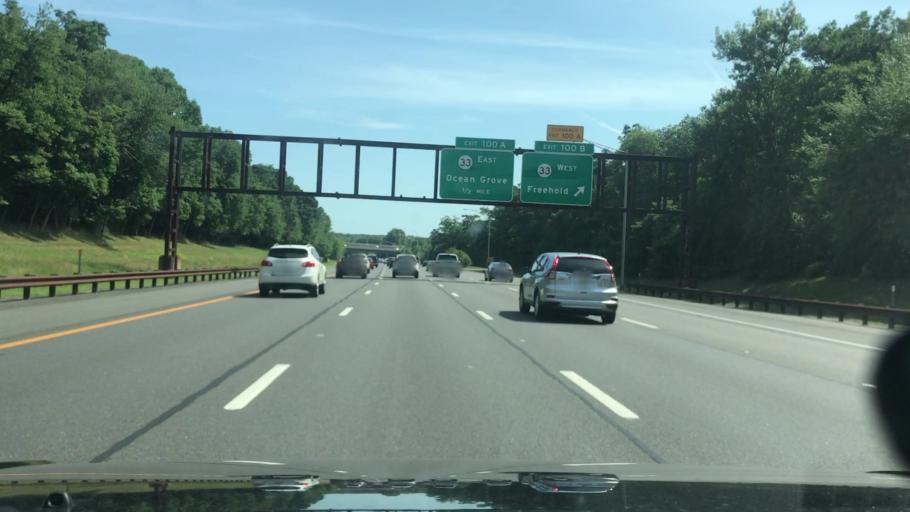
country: US
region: New Jersey
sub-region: Monmouth County
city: Shark River Hills
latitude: 40.2227
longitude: -74.0987
